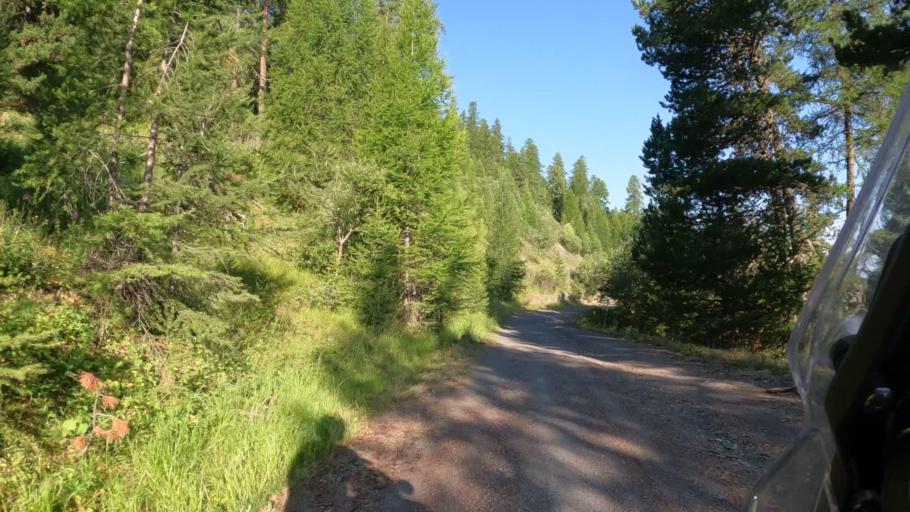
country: FR
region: Provence-Alpes-Cote d'Azur
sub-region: Departement des Hautes-Alpes
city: Guillestre
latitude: 44.6172
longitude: 6.6456
